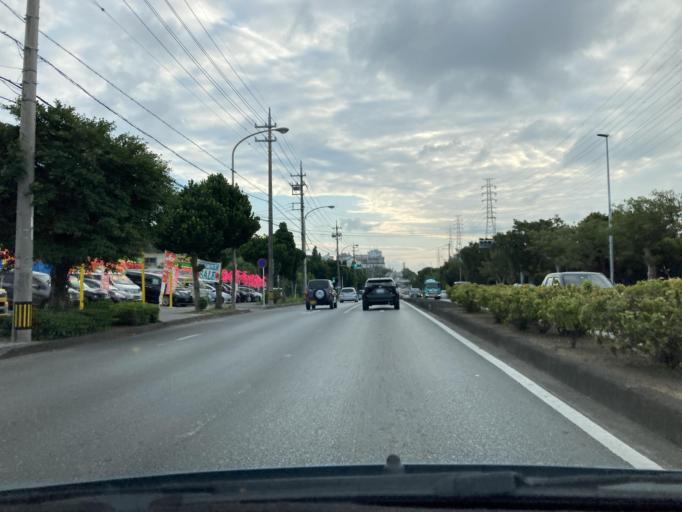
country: JP
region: Okinawa
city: Okinawa
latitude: 26.3475
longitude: 127.8019
